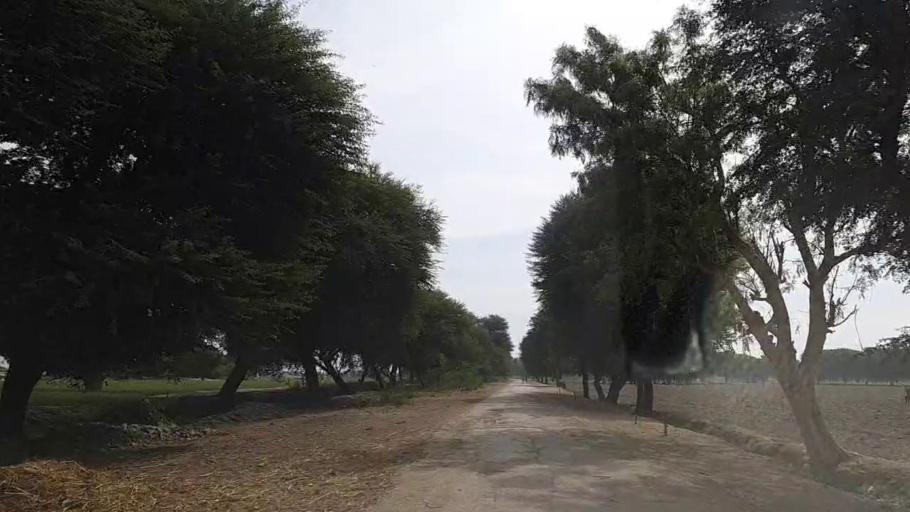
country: PK
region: Sindh
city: Samaro
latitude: 25.2862
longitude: 69.4191
